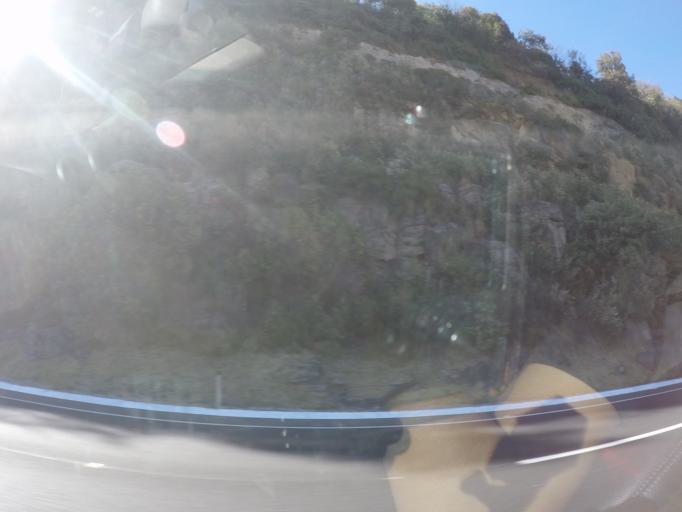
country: MX
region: Mexico City
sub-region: Cuajimalpa de Morelos
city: San Lorenzo Acopilco
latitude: 19.3167
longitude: -99.3380
